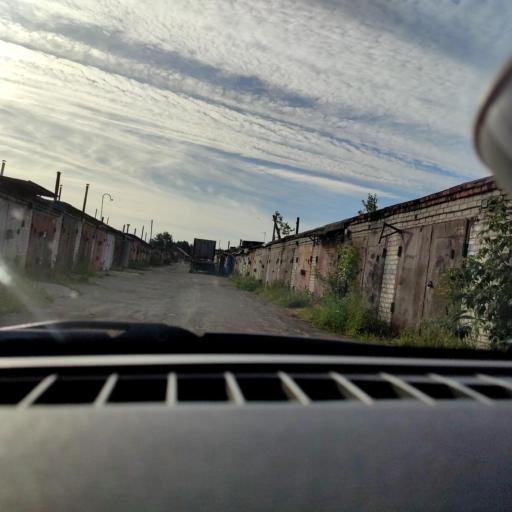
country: RU
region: Perm
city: Kondratovo
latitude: 57.9574
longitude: 56.1681
